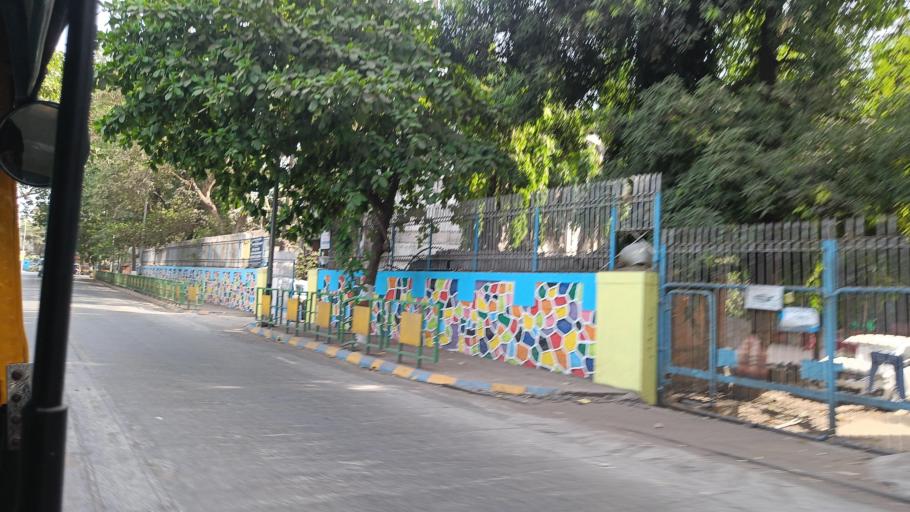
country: IN
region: Maharashtra
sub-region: Thane
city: Thane
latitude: 19.1800
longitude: 72.9679
